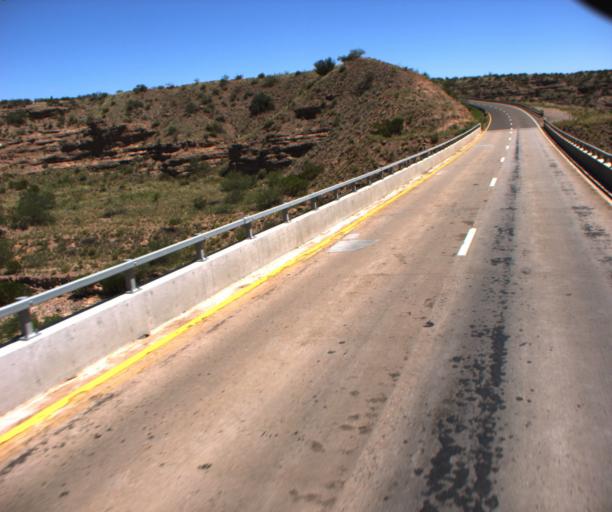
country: US
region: Arizona
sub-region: Greenlee County
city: Clifton
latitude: 32.9713
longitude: -109.2409
